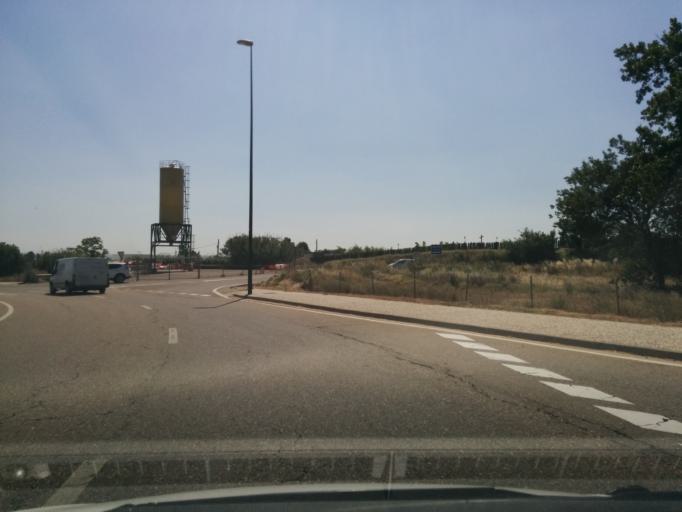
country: ES
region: Aragon
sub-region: Provincia de Zaragoza
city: Zaragoza
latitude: 41.6205
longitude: -0.8618
